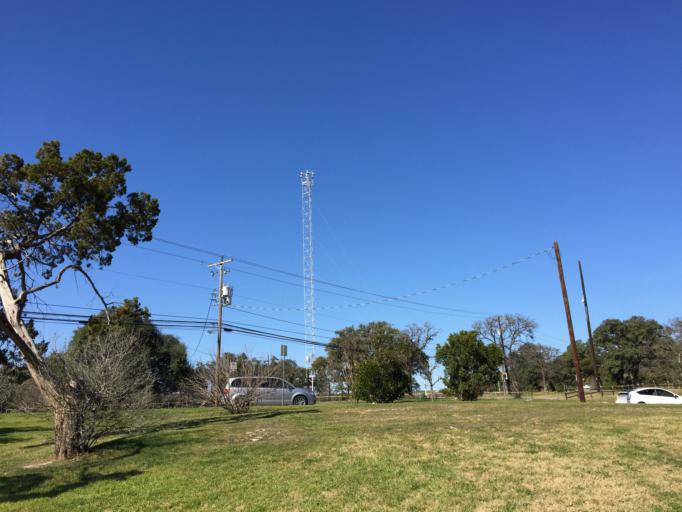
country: US
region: Texas
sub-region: Travis County
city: Rollingwood
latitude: 30.2659
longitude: -97.7701
